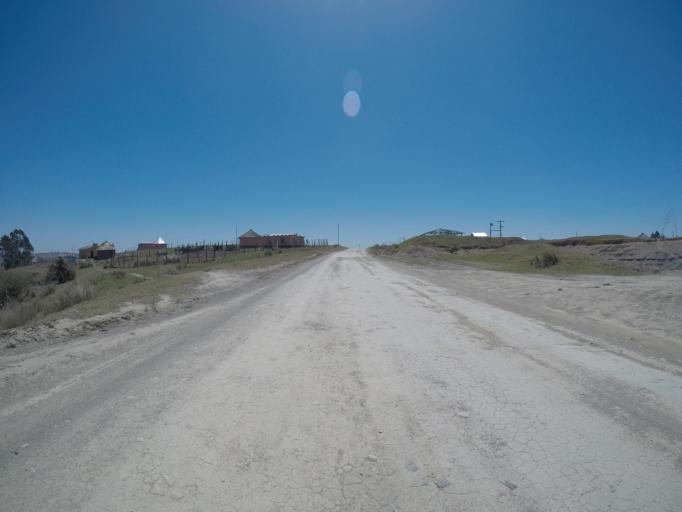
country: ZA
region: Eastern Cape
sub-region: OR Tambo District Municipality
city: Libode
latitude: -31.9422
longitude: 29.0272
